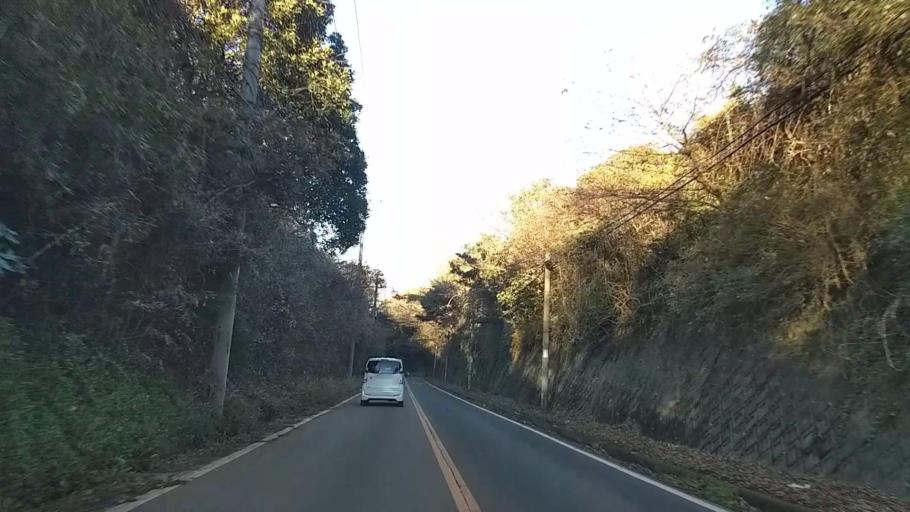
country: JP
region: Chiba
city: Hasaki
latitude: 35.7613
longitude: 140.7497
